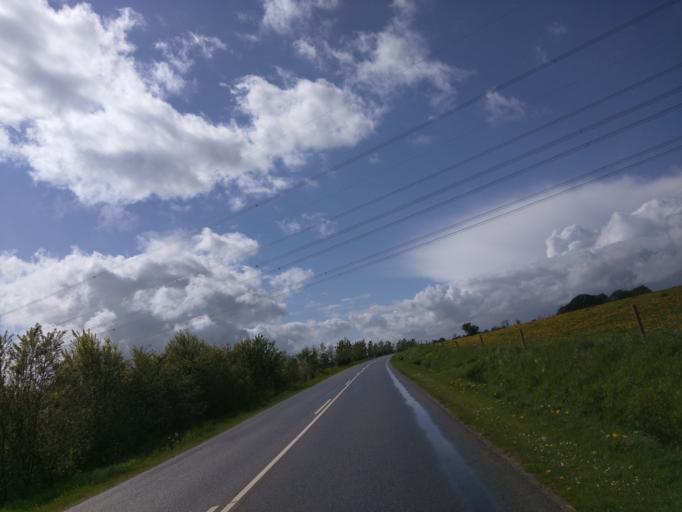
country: DK
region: Central Jutland
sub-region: Silkeborg Kommune
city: Kjellerup
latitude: 56.2789
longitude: 9.4904
